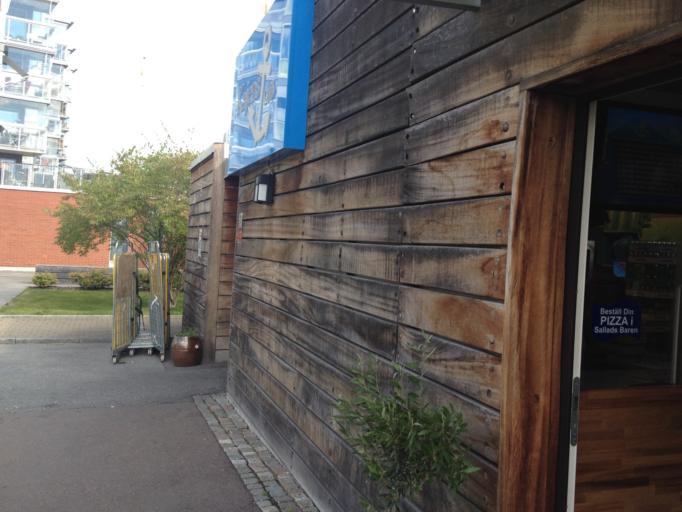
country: SE
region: Vaestmanland
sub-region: Vasteras
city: Vasteras
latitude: 59.6036
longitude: 16.5509
